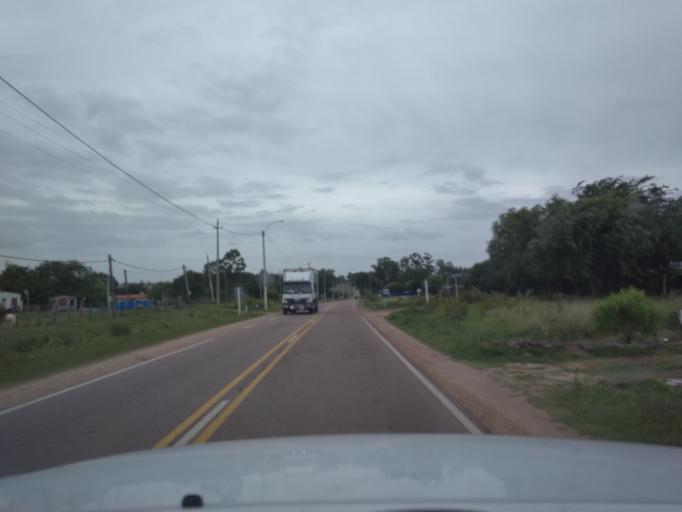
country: UY
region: Canelones
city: Tala
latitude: -34.3518
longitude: -55.7686
